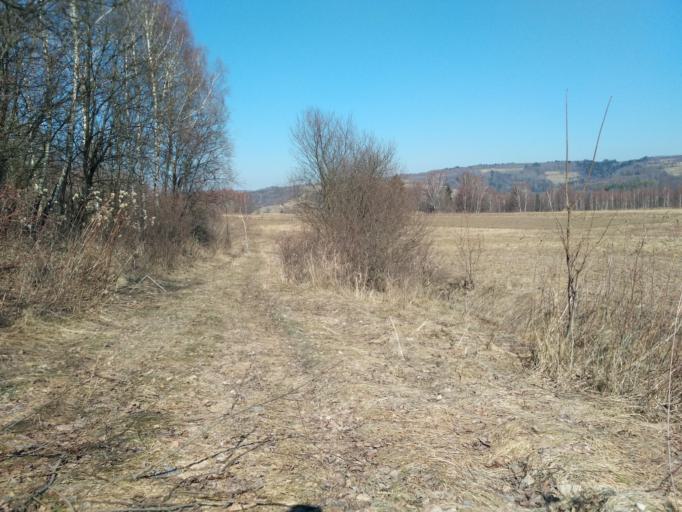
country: PL
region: Subcarpathian Voivodeship
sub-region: Powiat brzozowski
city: Golcowa
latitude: 49.7616
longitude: 22.0315
